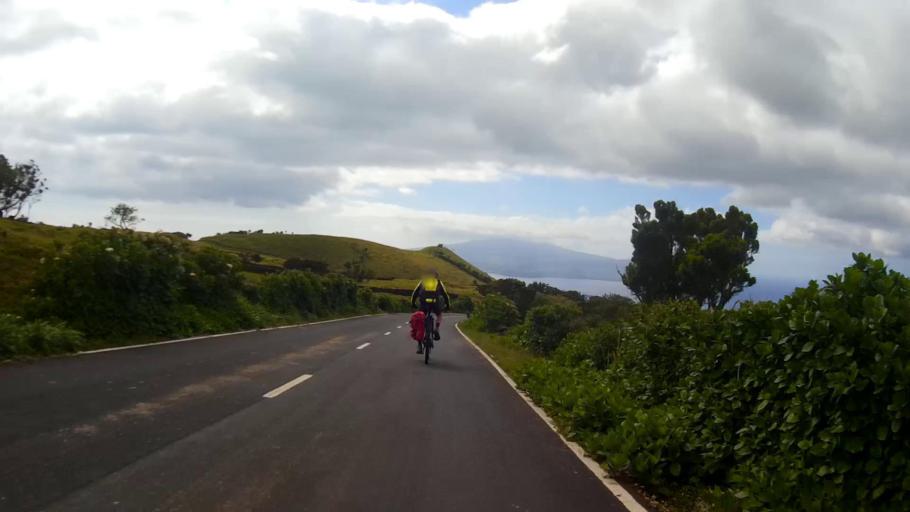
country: PT
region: Azores
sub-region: Madalena
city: Madalena
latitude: 38.4964
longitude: -28.4592
